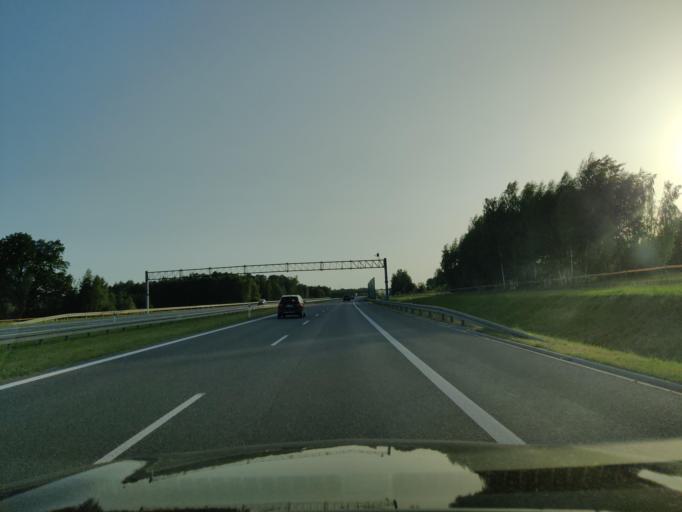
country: PL
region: Masovian Voivodeship
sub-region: Powiat minski
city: Minsk Mazowiecki
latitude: 52.2056
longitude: 21.5122
